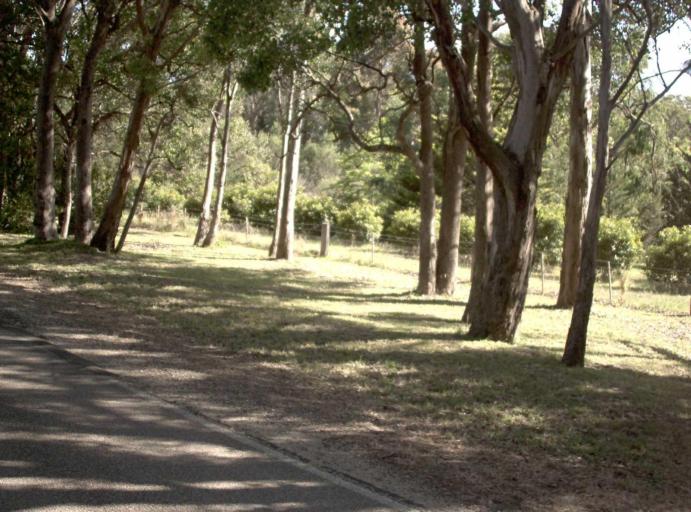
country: AU
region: Victoria
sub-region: East Gippsland
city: Lakes Entrance
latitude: -37.7860
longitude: 147.8286
